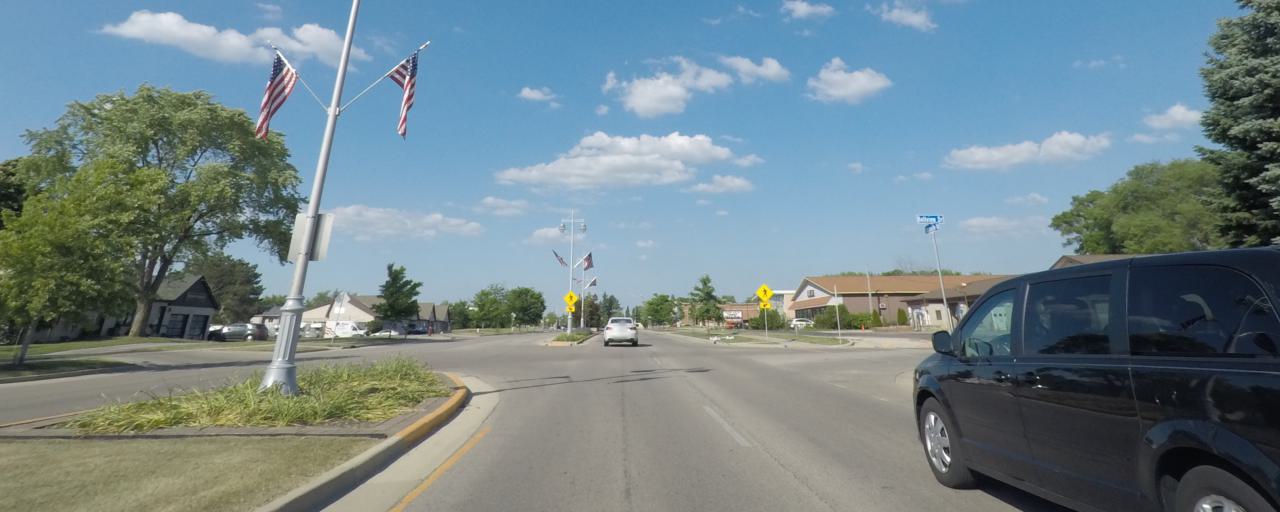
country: US
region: Wisconsin
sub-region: Waukesha County
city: Muskego
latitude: 42.9115
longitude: -88.1220
